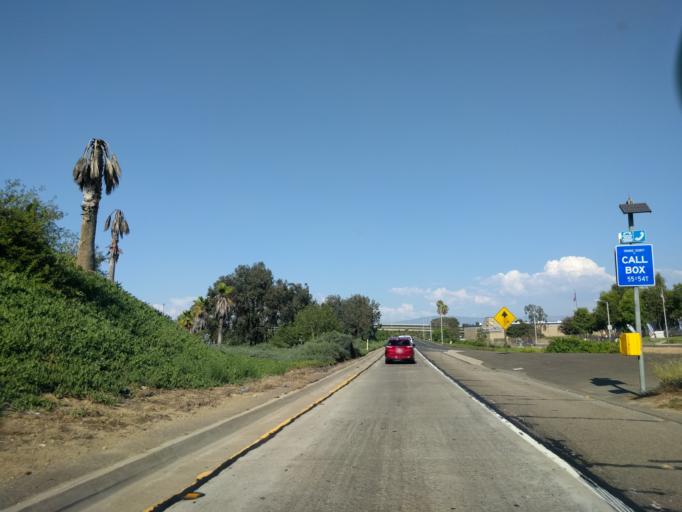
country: US
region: California
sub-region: Orange County
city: Irvine
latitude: 33.6851
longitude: -117.8736
